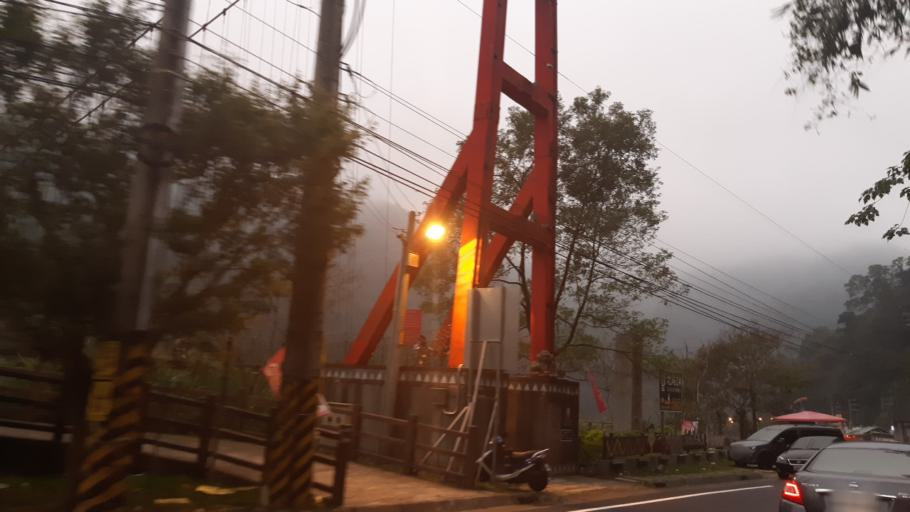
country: TW
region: Taiwan
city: Daxi
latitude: 24.7023
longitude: 121.1975
